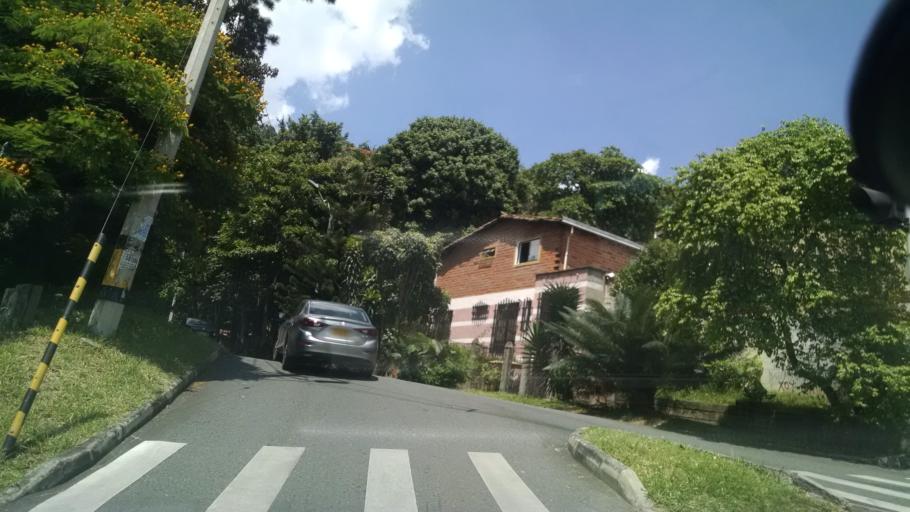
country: CO
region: Antioquia
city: Itagui
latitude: 6.2223
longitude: -75.5979
